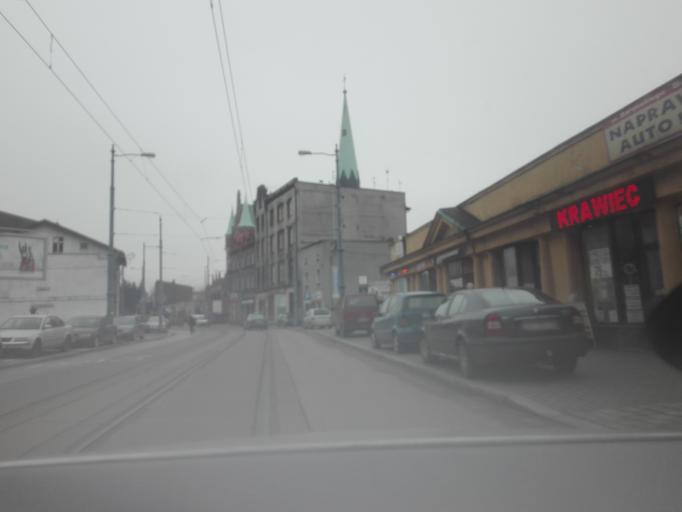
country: PL
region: Silesian Voivodeship
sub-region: Katowice
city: Katowice
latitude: 50.2645
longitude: 18.9990
